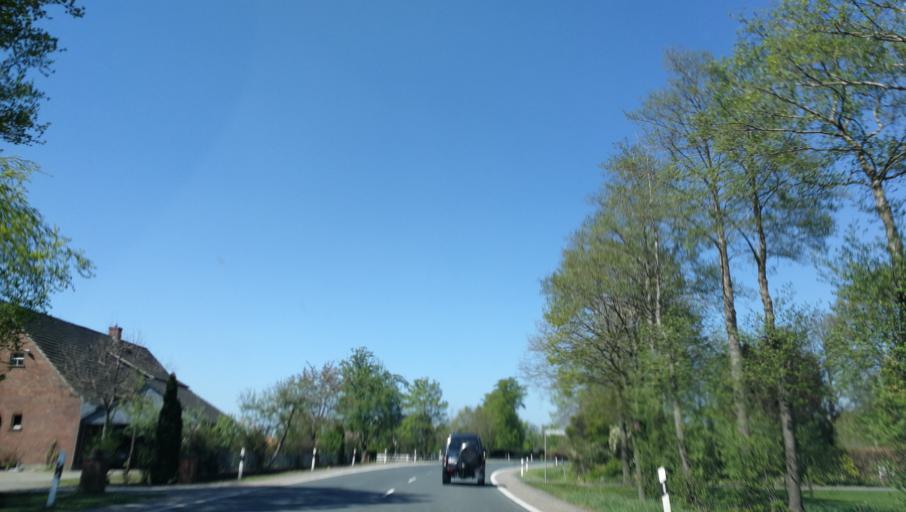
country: DE
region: North Rhine-Westphalia
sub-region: Regierungsbezirk Munster
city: Wettringen
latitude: 52.1941
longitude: 7.3246
